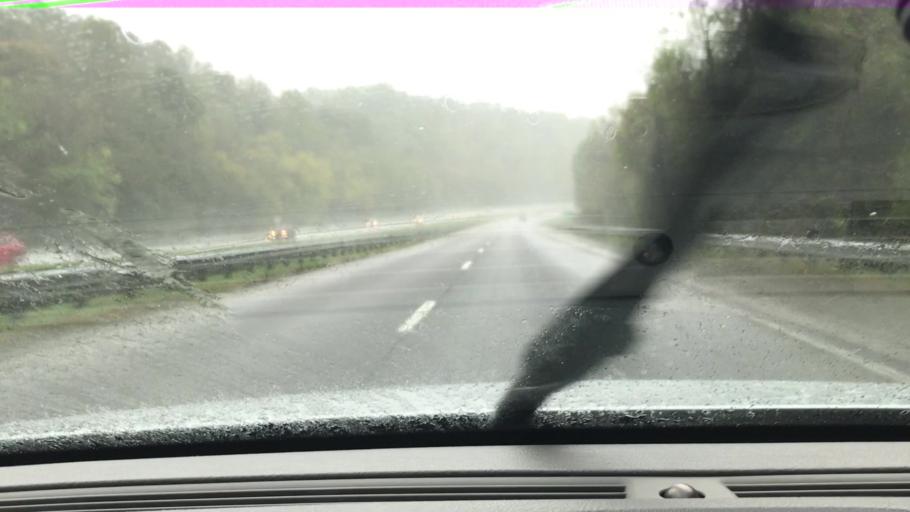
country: US
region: Alabama
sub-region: Limestone County
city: Ardmore
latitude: 34.9829
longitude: -86.8797
